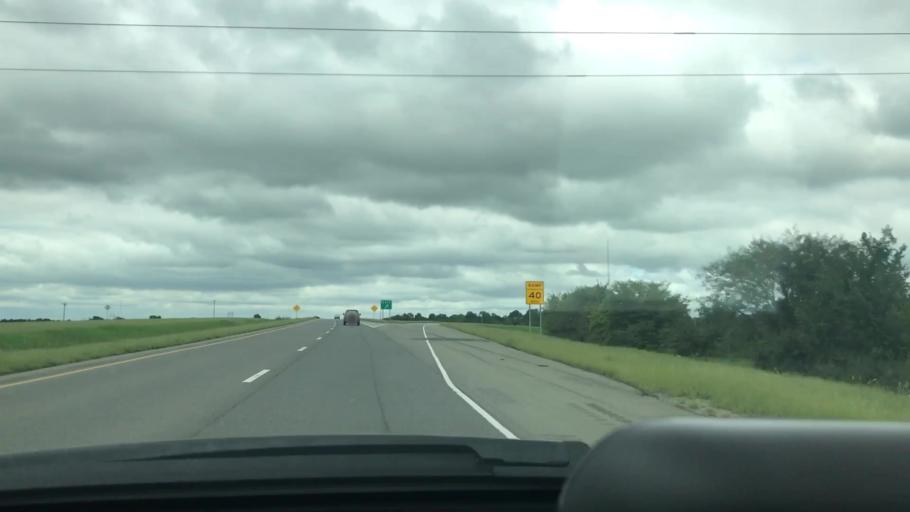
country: US
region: Oklahoma
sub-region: McIntosh County
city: Checotah
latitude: 35.5725
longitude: -95.4909
